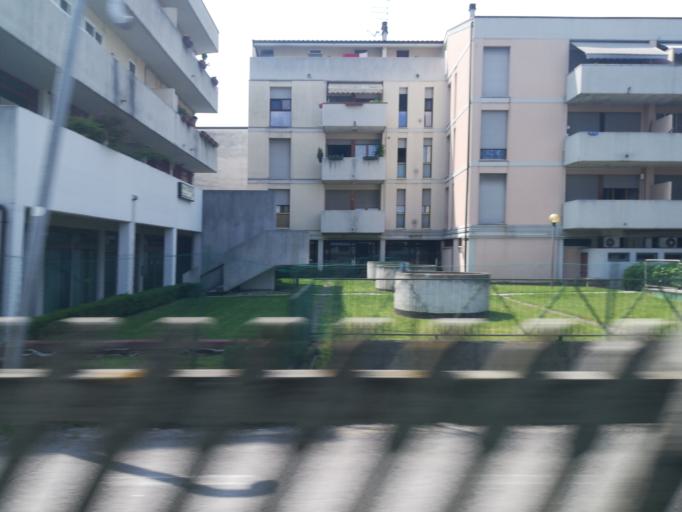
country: IT
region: Veneto
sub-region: Provincia di Vicenza
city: Monticello Conte Otto
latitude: 45.6001
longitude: 11.5701
